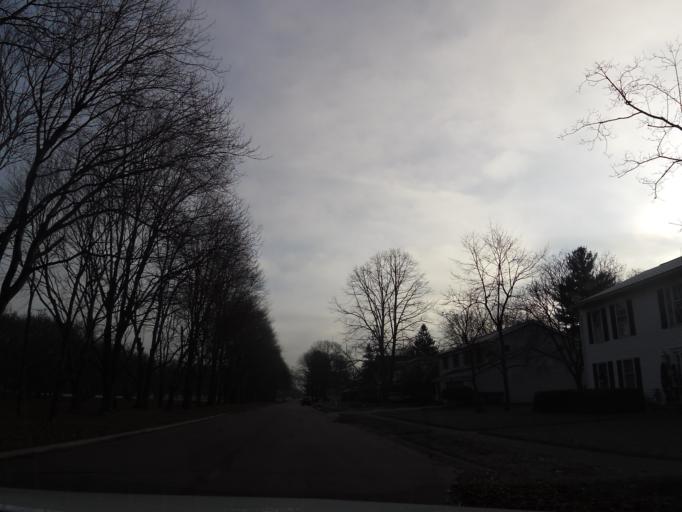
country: US
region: Indiana
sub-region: Bartholomew County
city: Columbus
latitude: 39.2289
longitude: -85.9169
